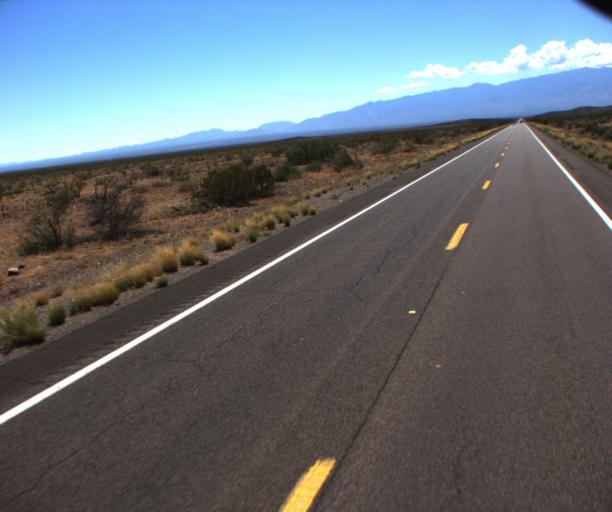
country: US
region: Arizona
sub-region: Graham County
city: Safford
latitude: 32.8158
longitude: -109.4889
